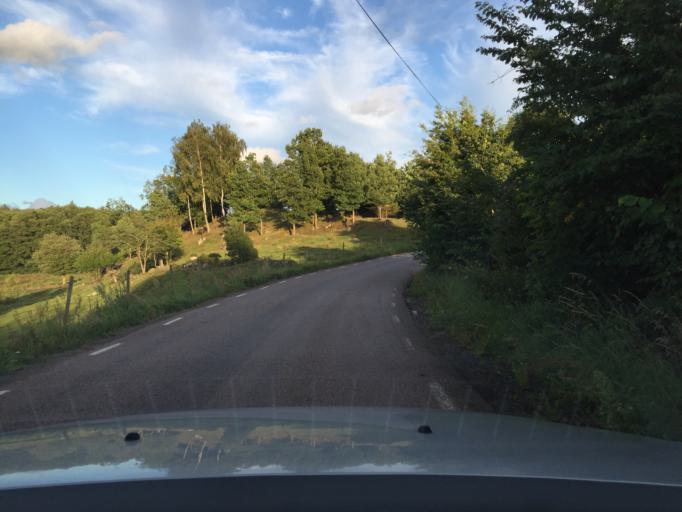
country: SE
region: Skane
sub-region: Hassleholms Kommun
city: Tormestorp
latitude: 56.0240
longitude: 13.7698
